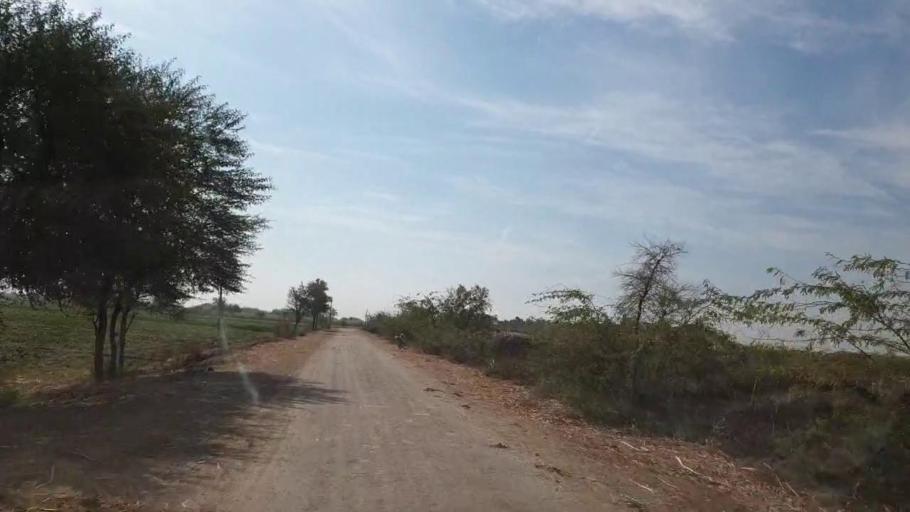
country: PK
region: Sindh
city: Mirpur Khas
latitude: 25.5278
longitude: 69.1551
